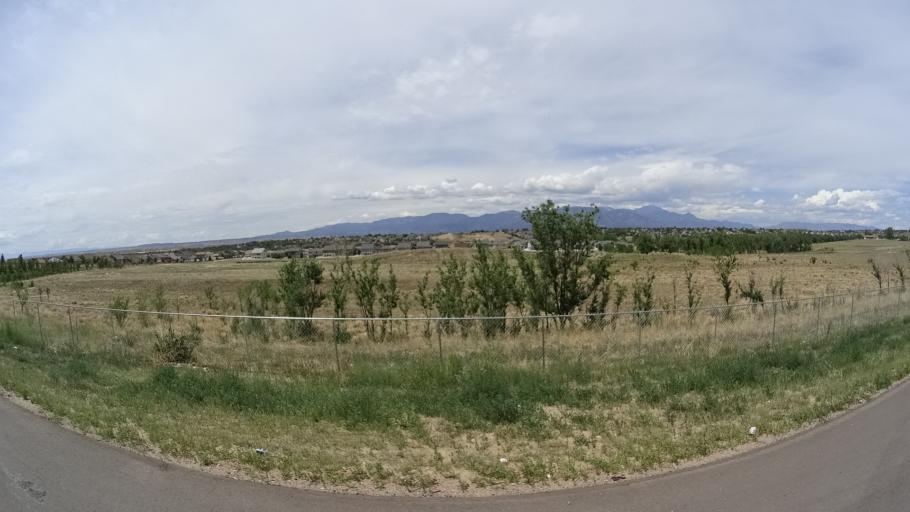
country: US
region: Colorado
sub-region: El Paso County
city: Fountain
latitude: 38.6958
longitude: -104.6737
